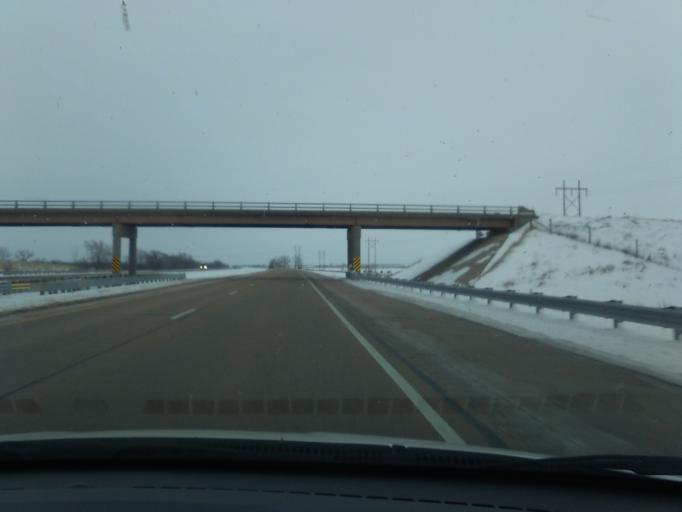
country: US
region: Nebraska
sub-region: Keith County
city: Ogallala
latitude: 41.0955
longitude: -101.8080
